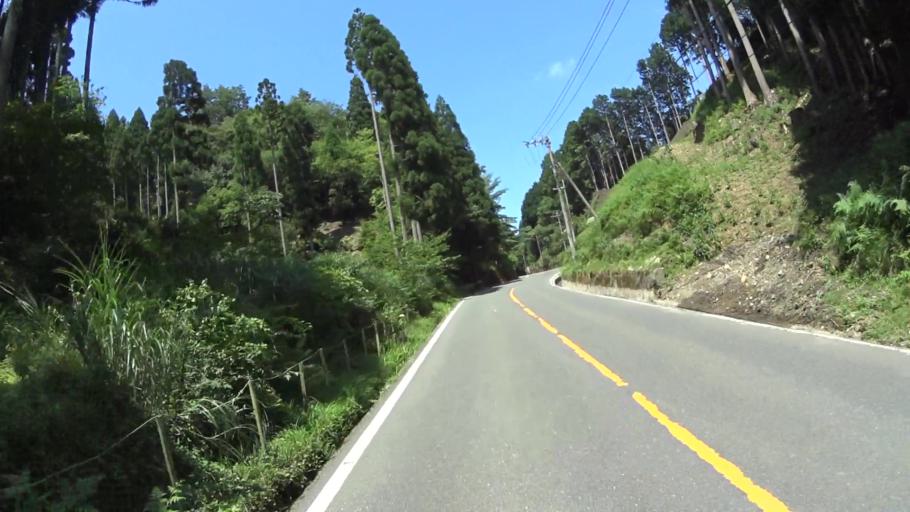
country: JP
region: Fukui
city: Obama
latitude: 35.3860
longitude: 135.9257
